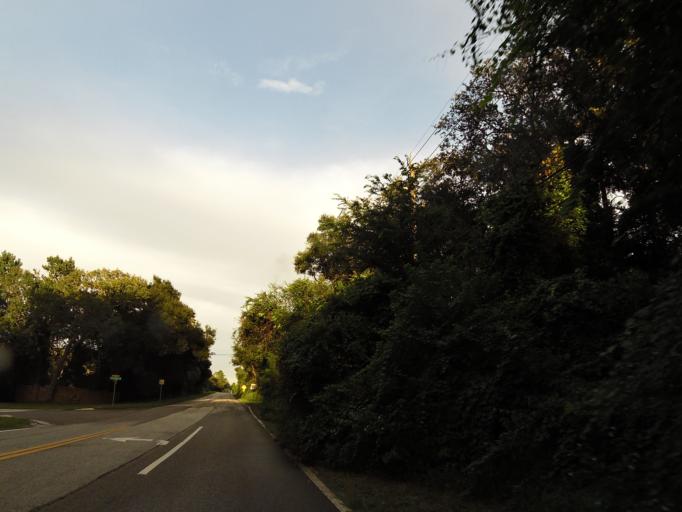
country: US
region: Florida
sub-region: Duval County
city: Atlantic Beach
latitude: 30.3794
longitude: -81.4992
